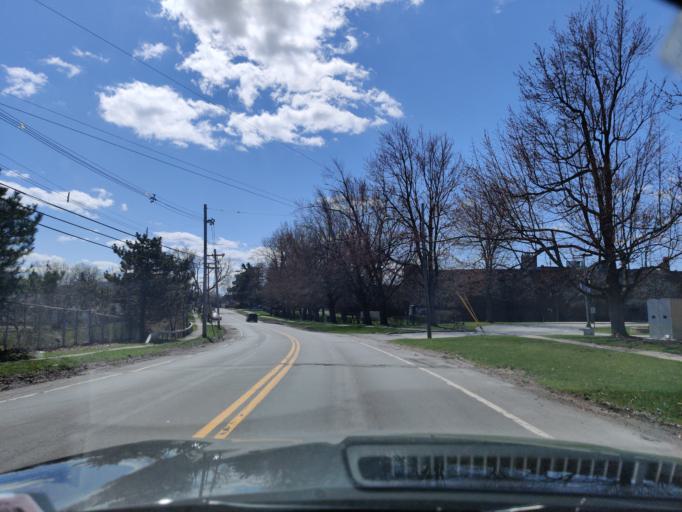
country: US
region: New York
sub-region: Erie County
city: Sloan
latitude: 42.9121
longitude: -78.7962
